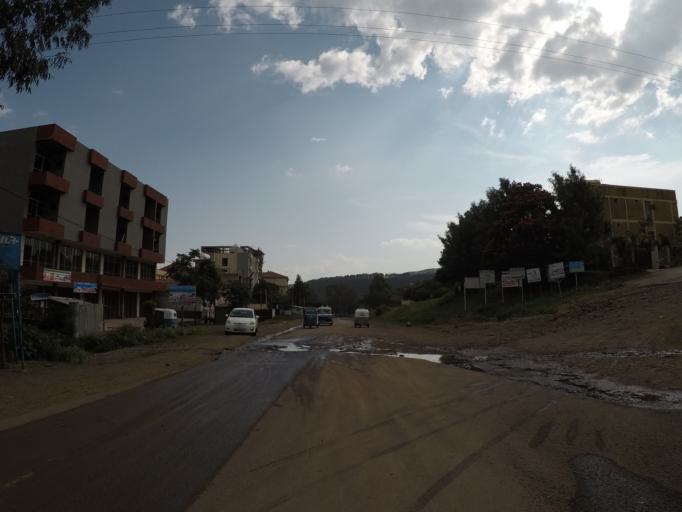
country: ET
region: Amhara
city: Gondar
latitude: 12.5892
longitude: 37.4396
